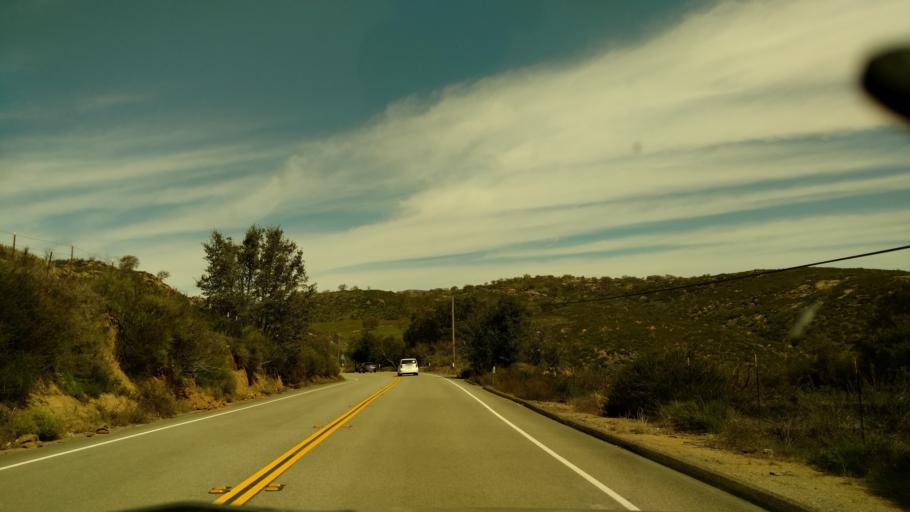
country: US
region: California
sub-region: San Diego County
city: San Diego Country Estates
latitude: 33.0670
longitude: -116.7227
